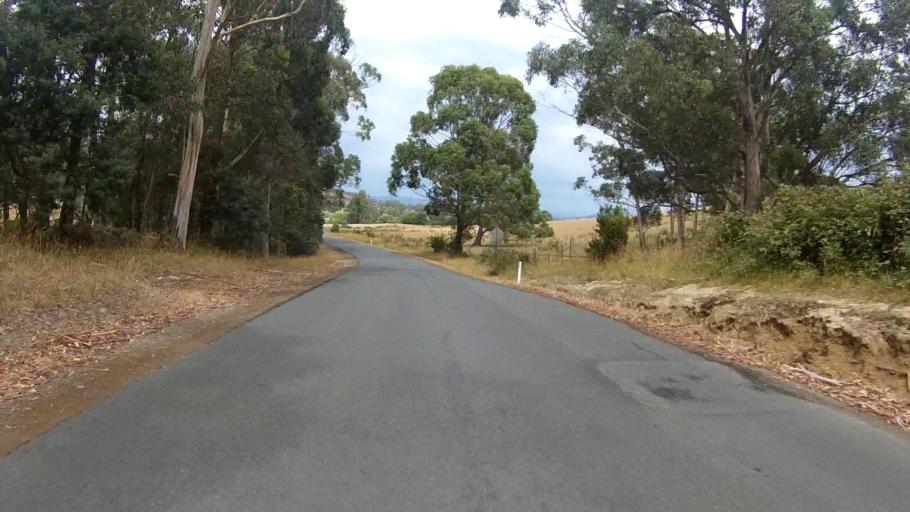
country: AU
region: Tasmania
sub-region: Huon Valley
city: Cygnet
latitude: -43.1815
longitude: 147.1128
